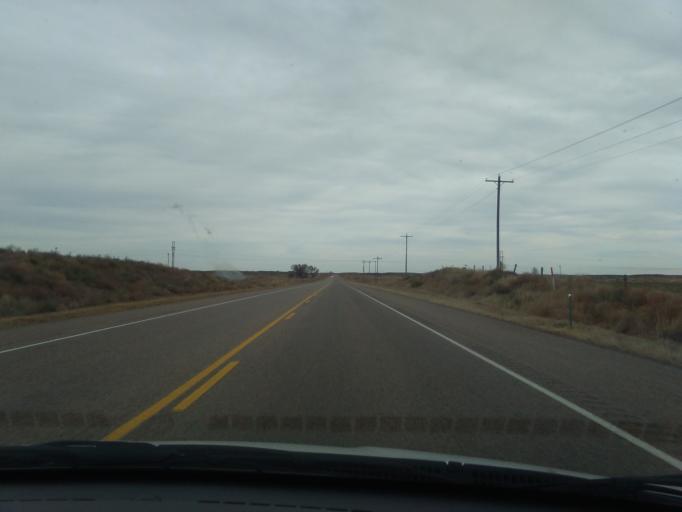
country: US
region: Colorado
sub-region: Yuma County
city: Yuma
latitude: 40.1089
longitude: -102.5527
